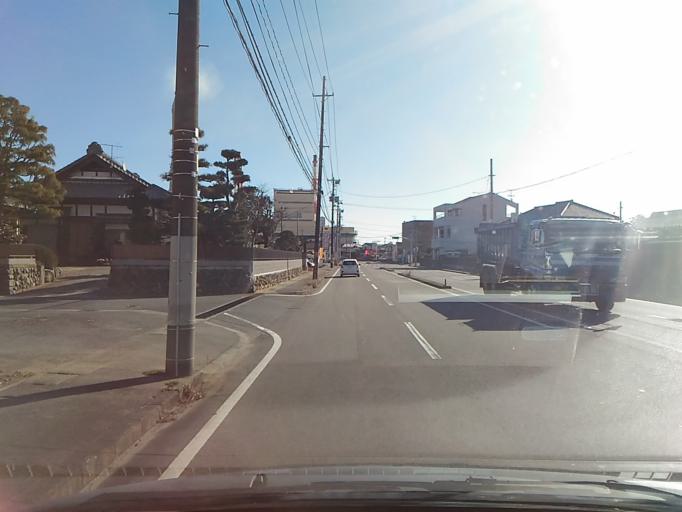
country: JP
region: Ibaraki
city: Kitaibaraki
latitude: 36.9162
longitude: 140.8056
